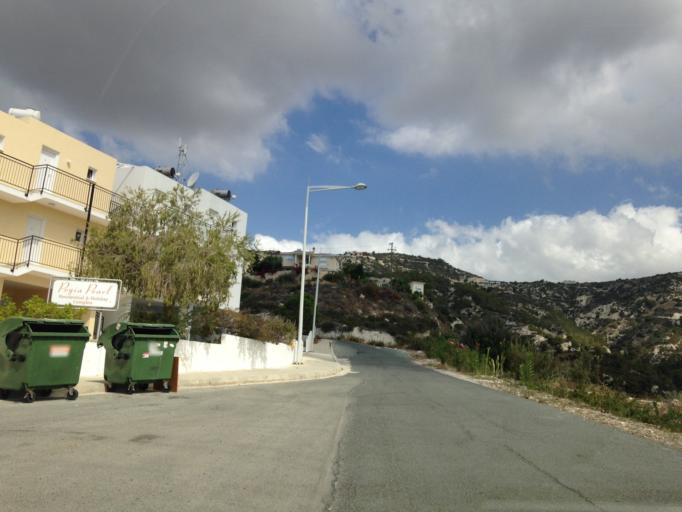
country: CY
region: Pafos
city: Pegeia
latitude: 34.8868
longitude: 32.3880
